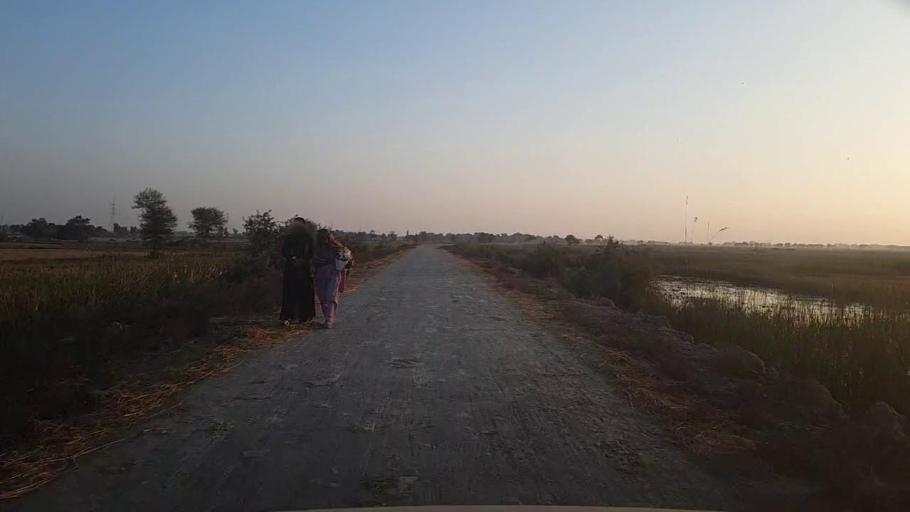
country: PK
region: Sindh
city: Khairpur Nathan Shah
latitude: 27.1779
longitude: 67.7340
